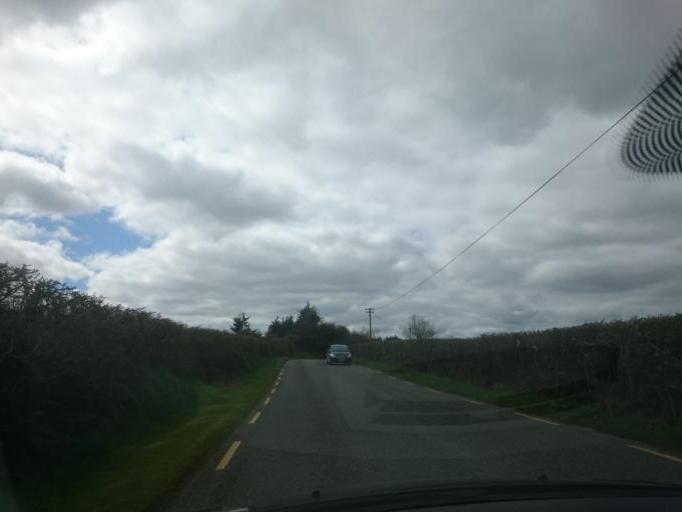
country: IE
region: Leinster
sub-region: Kilkenny
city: Callan
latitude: 52.6704
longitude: -7.3926
